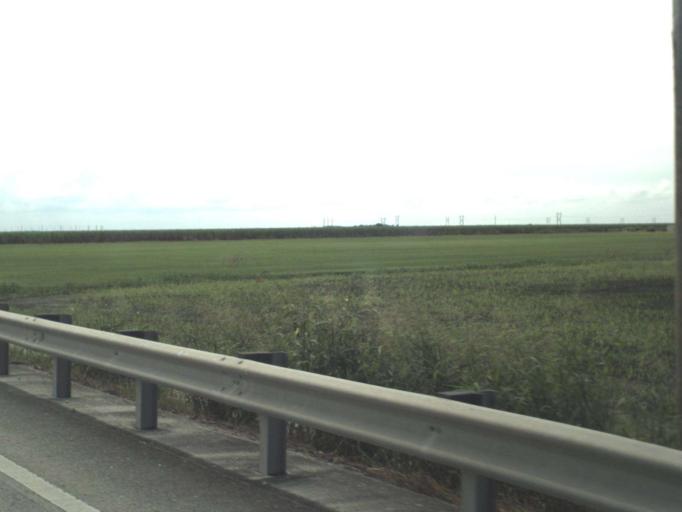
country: US
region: Florida
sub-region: Palm Beach County
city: Pahokee
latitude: 26.7822
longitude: -80.6534
